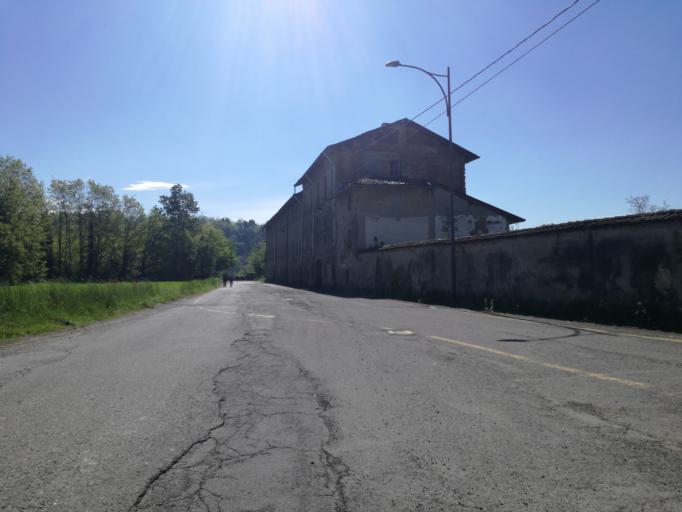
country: IT
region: Lombardy
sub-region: Provincia di Monza e Brianza
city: Porto d'Adda
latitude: 45.6633
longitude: 9.4832
